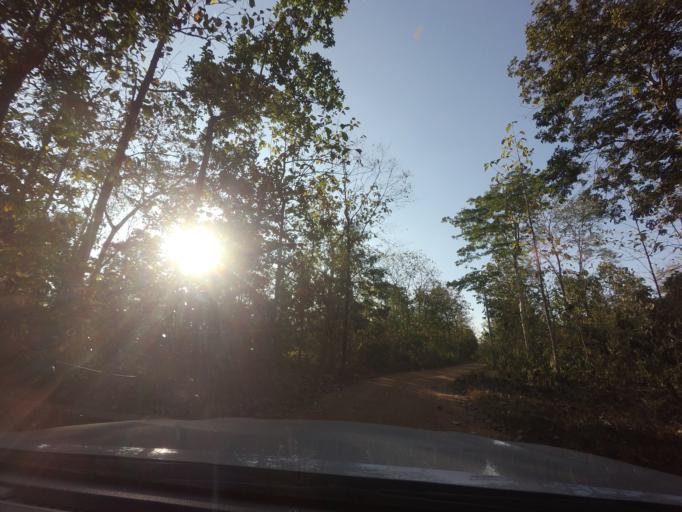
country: TH
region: Lampang
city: Mae Mo
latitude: 18.4139
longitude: 99.7438
